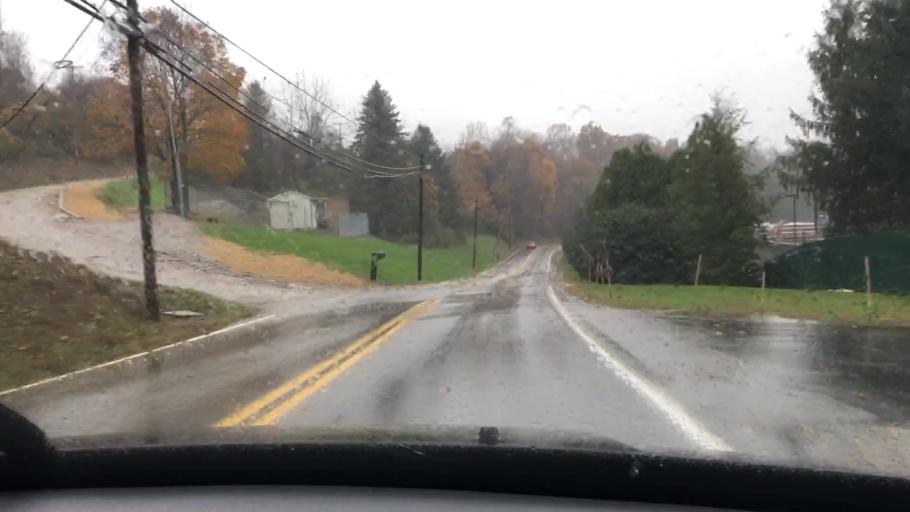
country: US
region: Pennsylvania
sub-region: York County
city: Shrewsbury
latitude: 39.7620
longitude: -76.7017
